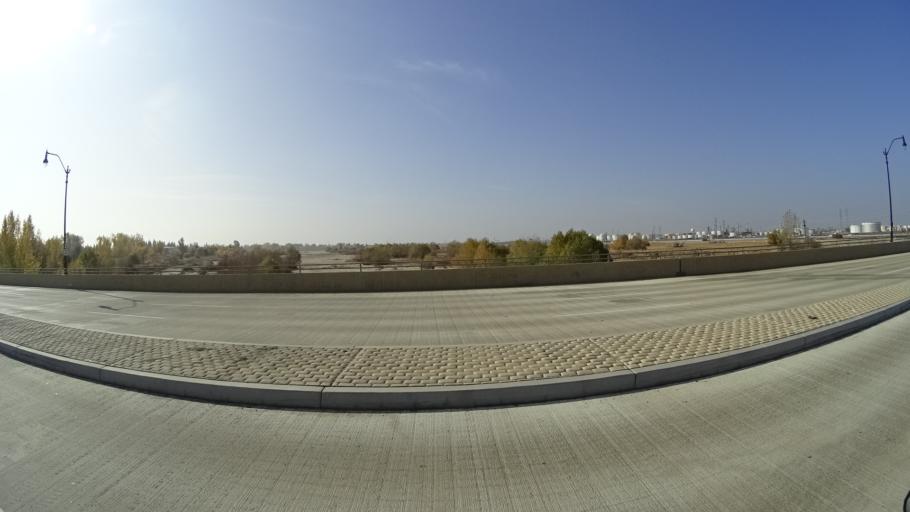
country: US
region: California
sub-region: Kern County
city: Greenacres
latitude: 35.3674
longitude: -119.0658
